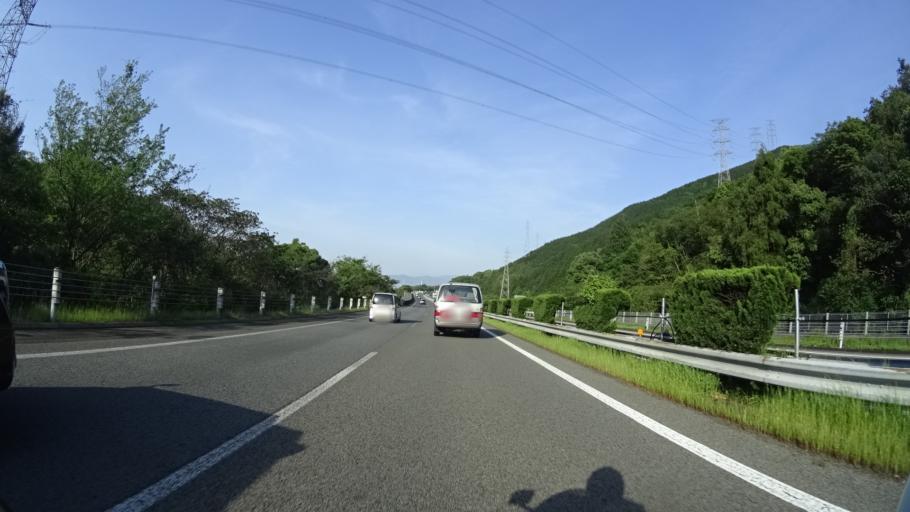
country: JP
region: Ehime
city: Niihama
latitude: 33.9425
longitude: 133.3998
